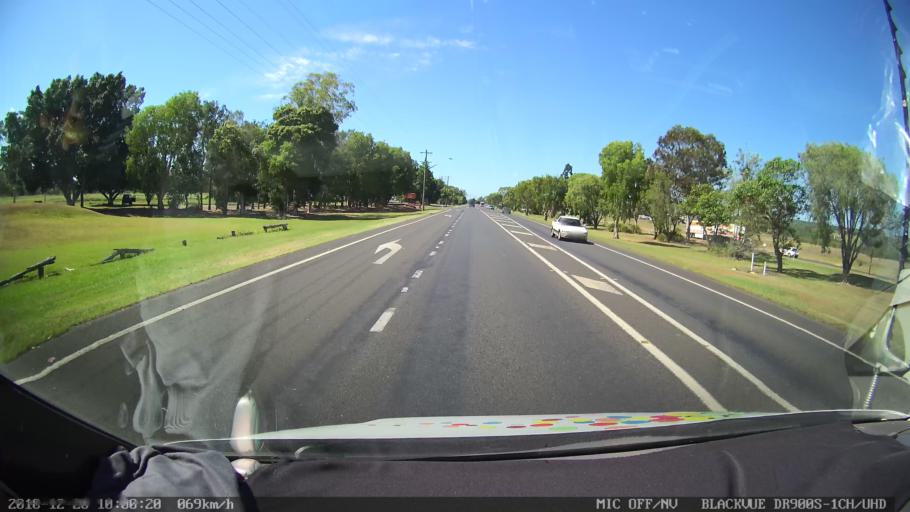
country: AU
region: New South Wales
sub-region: Lismore Municipality
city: Lismore
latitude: -28.8315
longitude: 153.2648
